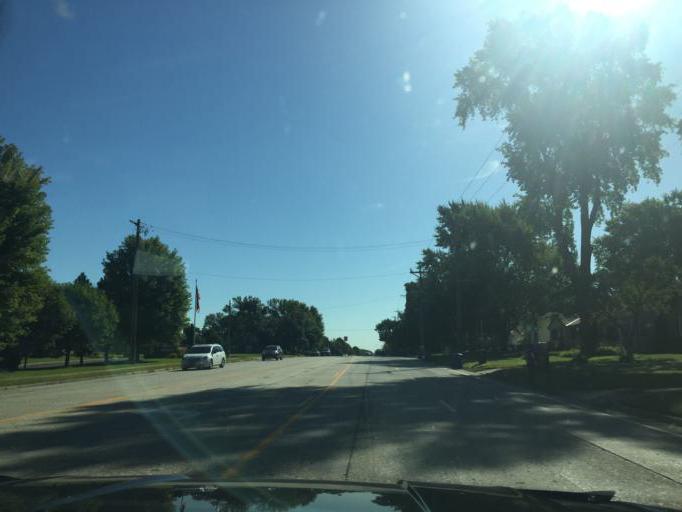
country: US
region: Minnesota
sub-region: Ramsey County
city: Roseville
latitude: 44.9920
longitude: -93.1442
